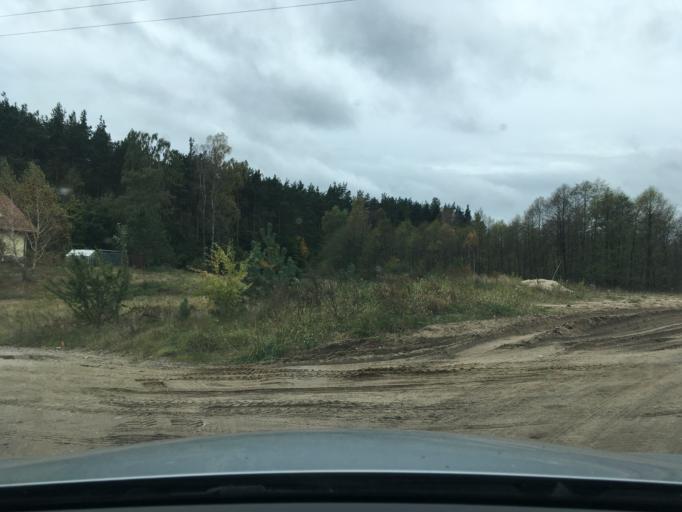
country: PL
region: Pomeranian Voivodeship
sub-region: Powiat koscierski
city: Koscierzyna
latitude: 54.1018
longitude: 17.9728
